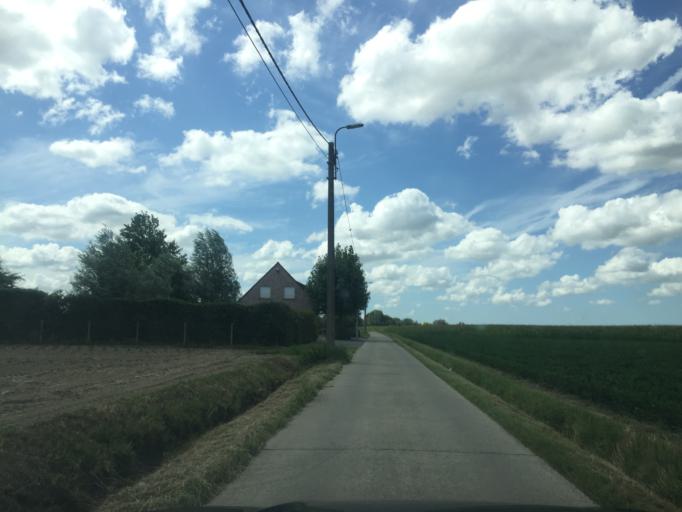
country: BE
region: Flanders
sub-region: Provincie West-Vlaanderen
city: Hooglede
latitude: 50.9472
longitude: 3.0568
